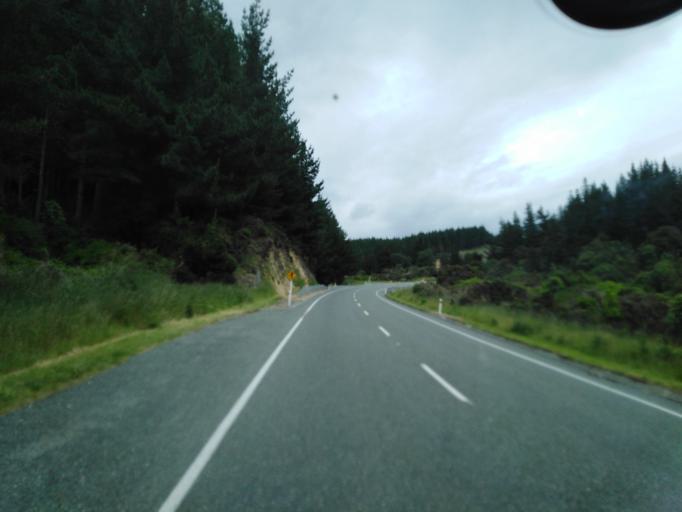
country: NZ
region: Tasman
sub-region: Tasman District
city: Wakefield
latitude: -41.4779
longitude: 172.9301
